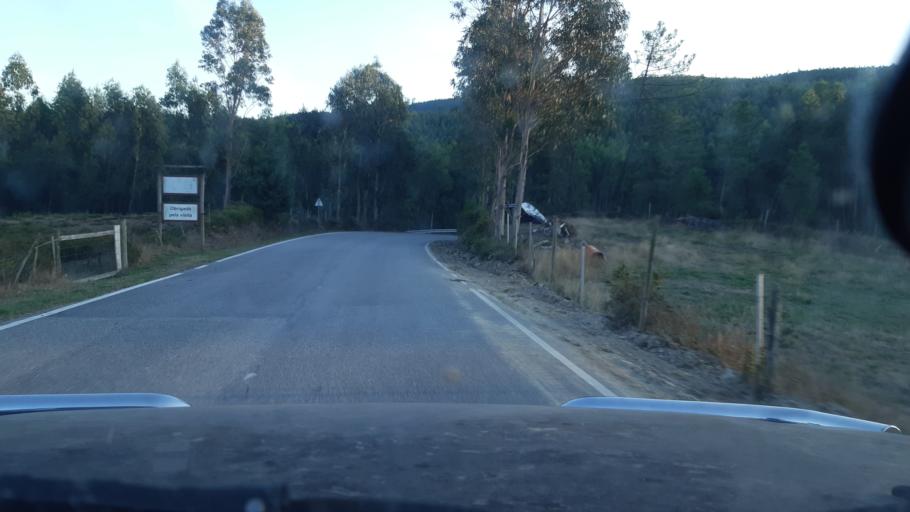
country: PT
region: Viseu
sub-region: Mortagua
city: Mortagua
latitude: 40.5442
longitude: -8.2639
